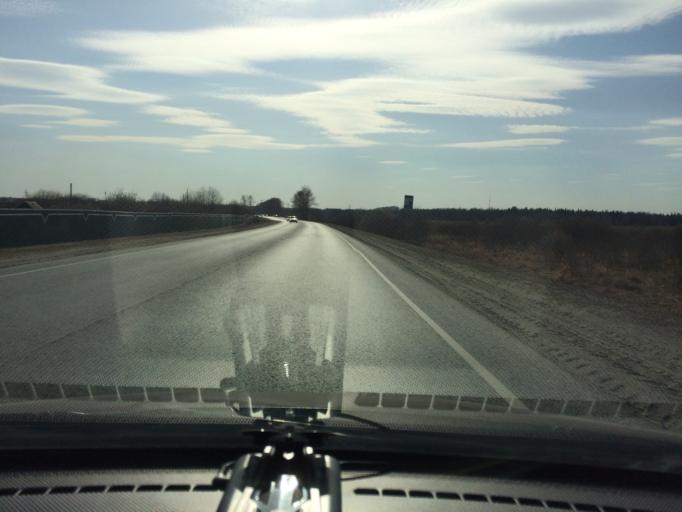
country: RU
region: Mariy-El
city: Yoshkar-Ola
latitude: 56.6559
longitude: 47.9601
